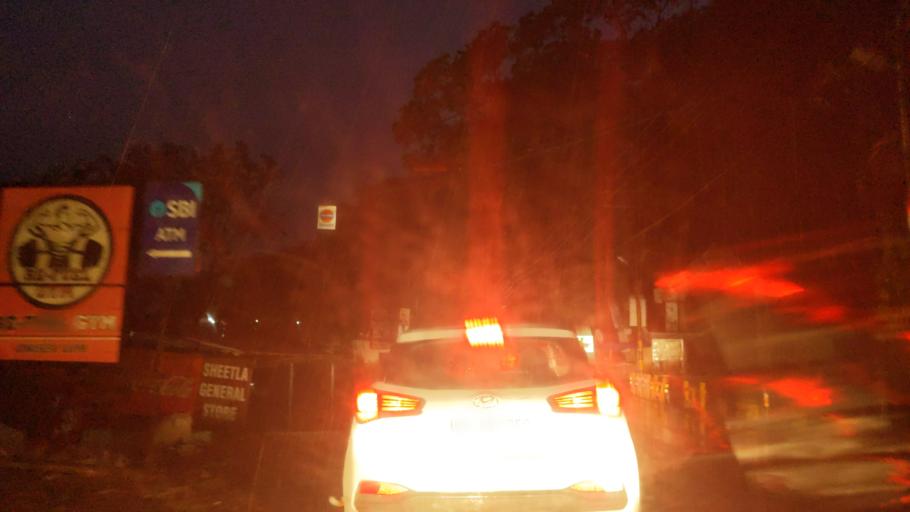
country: IN
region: Uttarakhand
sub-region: Naini Tal
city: Haldwani
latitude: 29.2826
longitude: 79.5451
